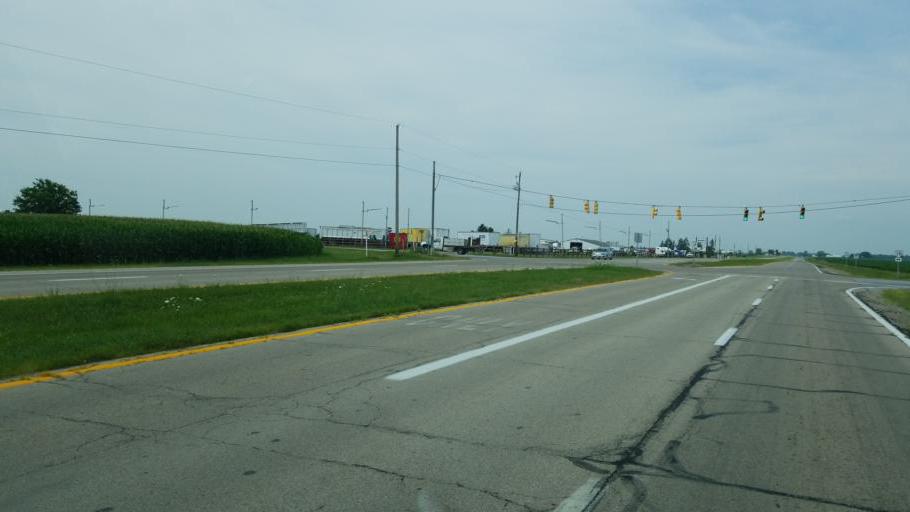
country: US
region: Ohio
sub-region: Madison County
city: Choctaw Lake
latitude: 39.9358
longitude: -83.4501
